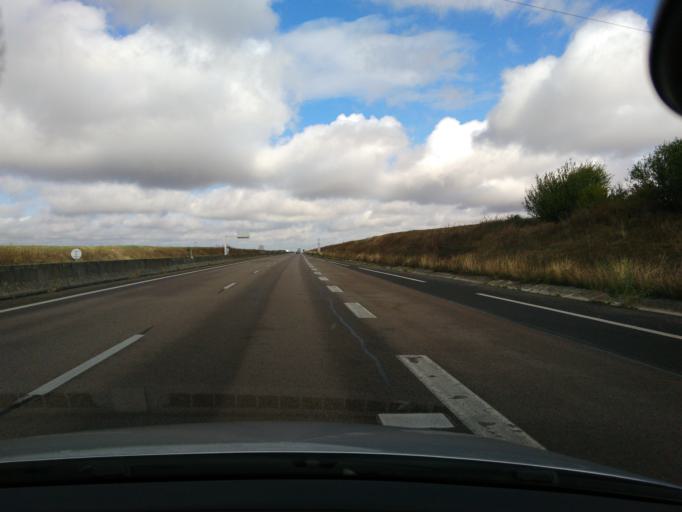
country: FR
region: Haute-Normandie
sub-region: Departement de l'Eure
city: La Madeleine-de-Nonancourt
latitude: 48.8365
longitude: 1.1829
